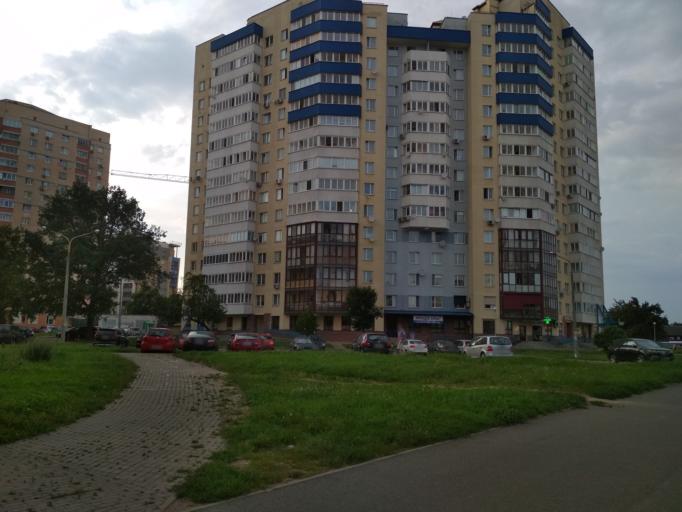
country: BY
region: Minsk
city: Minsk
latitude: 53.8841
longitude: 27.5505
